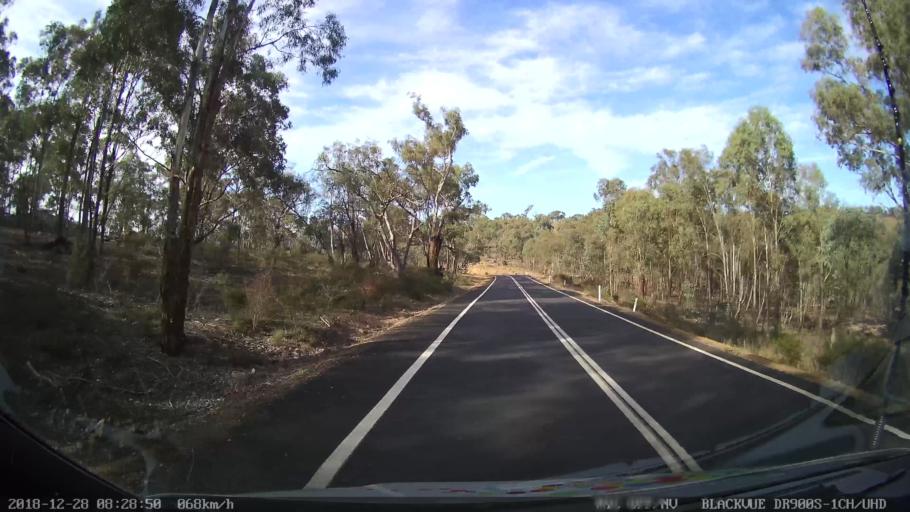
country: AU
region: New South Wales
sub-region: Blayney
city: Blayney
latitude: -33.9441
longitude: 149.3247
